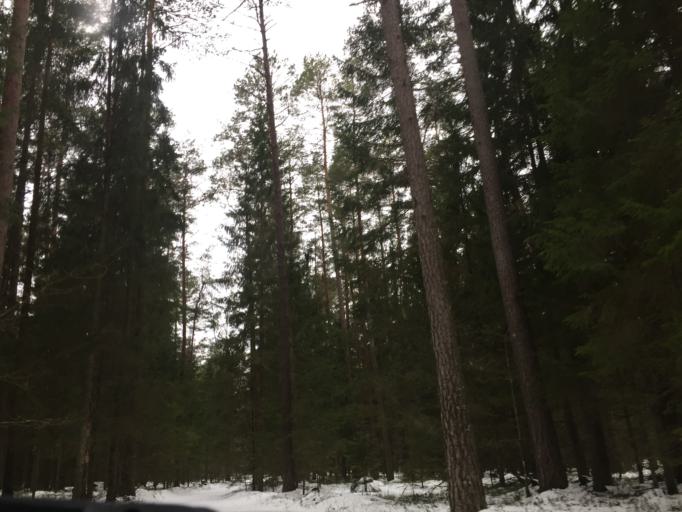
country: LV
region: Krimulda
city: Ragana
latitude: 57.1383
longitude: 24.7318
